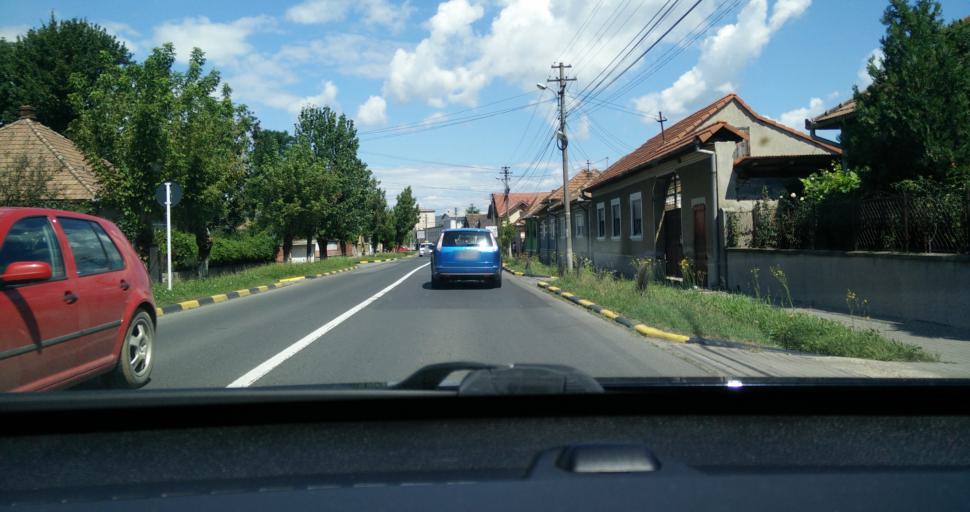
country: RO
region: Alba
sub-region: Municipiul Sebes
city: Sebes
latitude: 45.9478
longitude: 23.5650
